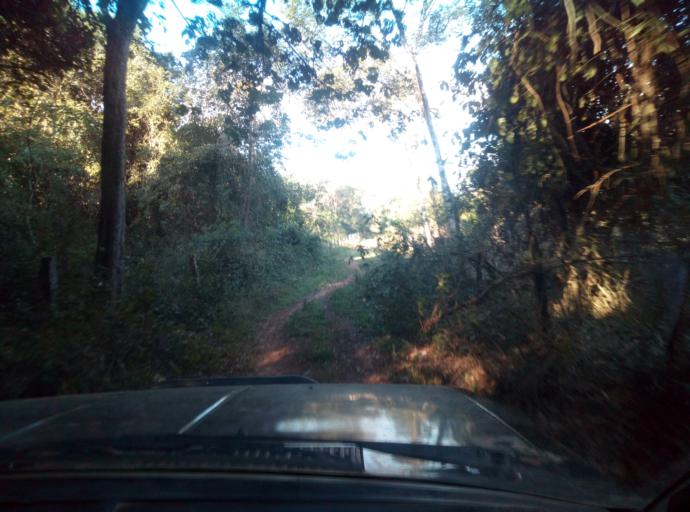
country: PY
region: Caaguazu
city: Carayao
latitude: -25.1752
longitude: -56.2675
